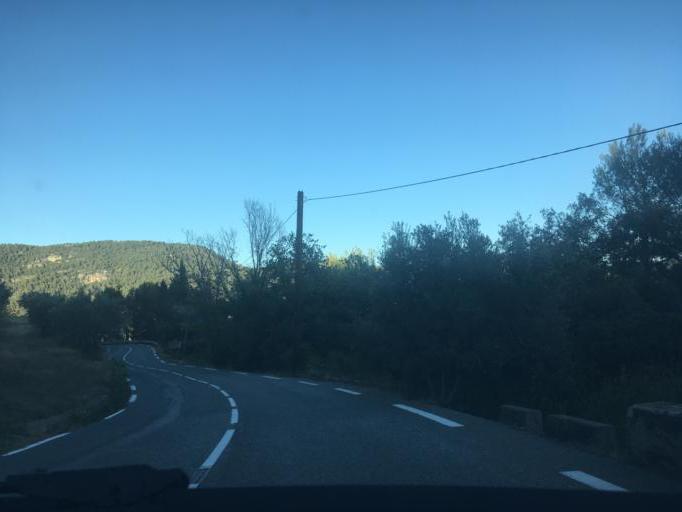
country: FR
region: Provence-Alpes-Cote d'Azur
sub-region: Departement du Var
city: Flayosc
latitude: 43.5636
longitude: 6.4124
